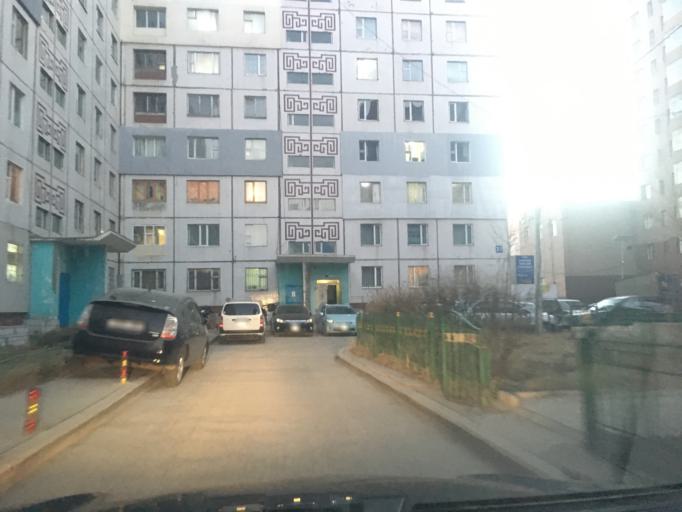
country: MN
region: Ulaanbaatar
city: Ulaanbaatar
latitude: 47.9192
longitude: 106.8901
